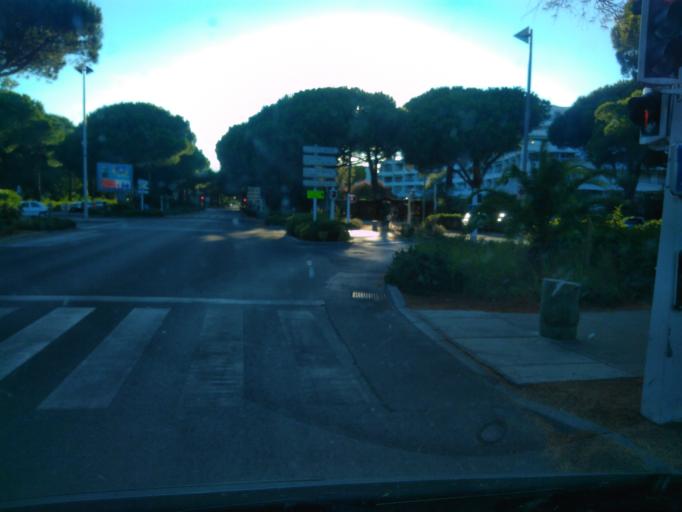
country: FR
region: Languedoc-Roussillon
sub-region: Departement de l'Herault
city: La Grande-Motte
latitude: 43.5616
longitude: 4.0720
